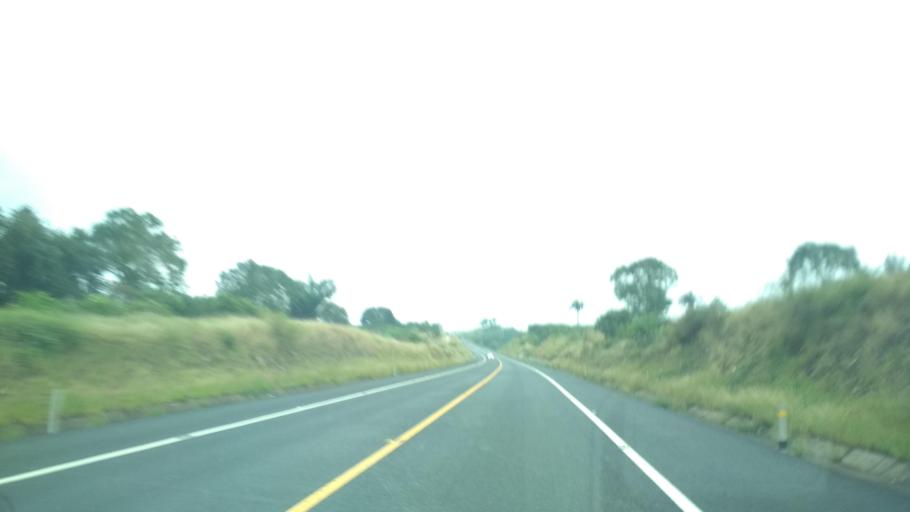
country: MX
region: Veracruz
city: Vega de San Marcos
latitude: 20.1814
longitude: -96.9654
